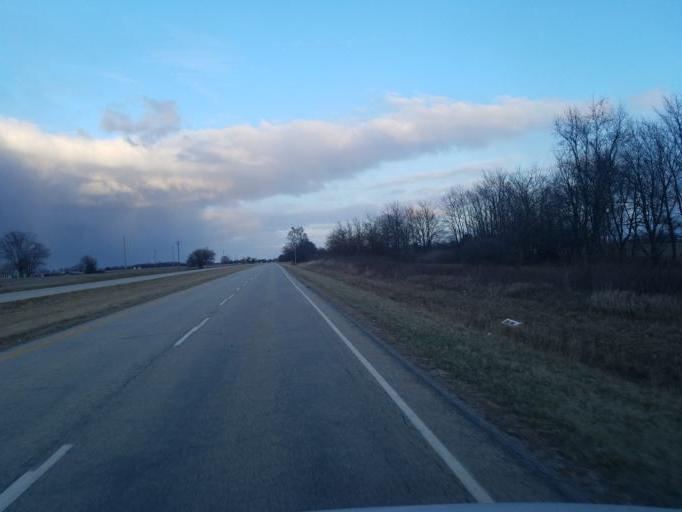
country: US
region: Indiana
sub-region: Henry County
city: Knightstown
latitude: 39.8021
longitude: -85.4645
